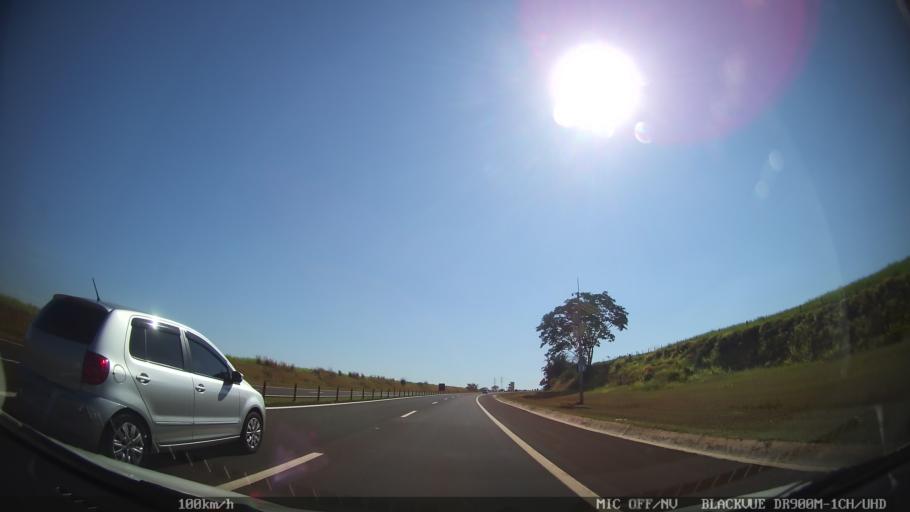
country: BR
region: Sao Paulo
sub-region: Ribeirao Preto
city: Ribeirao Preto
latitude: -21.1943
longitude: -47.8840
